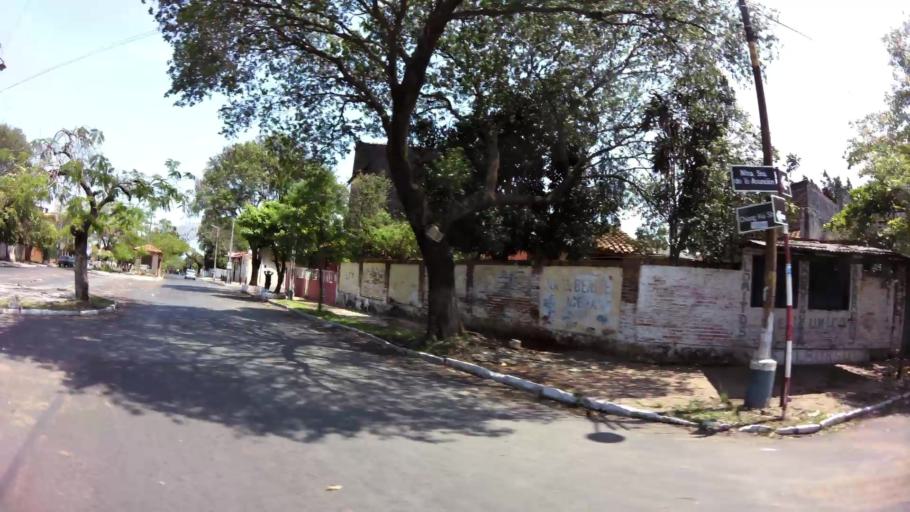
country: PY
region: Asuncion
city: Asuncion
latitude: -25.2999
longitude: -57.6464
